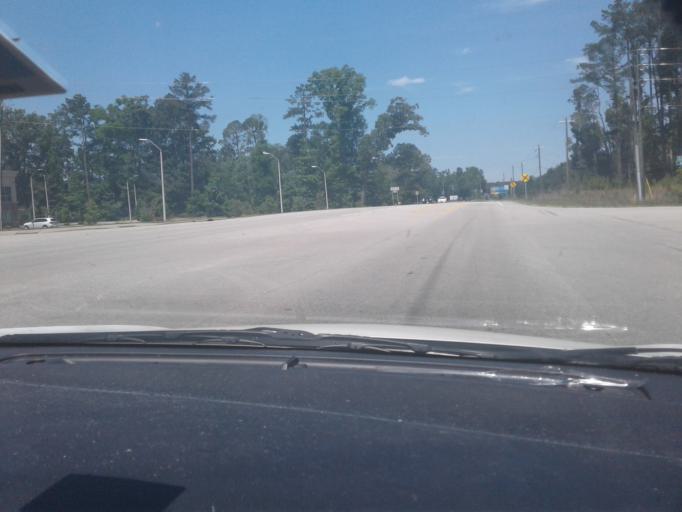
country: US
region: North Carolina
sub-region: Harnett County
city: Lillington
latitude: 35.4248
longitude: -78.8146
